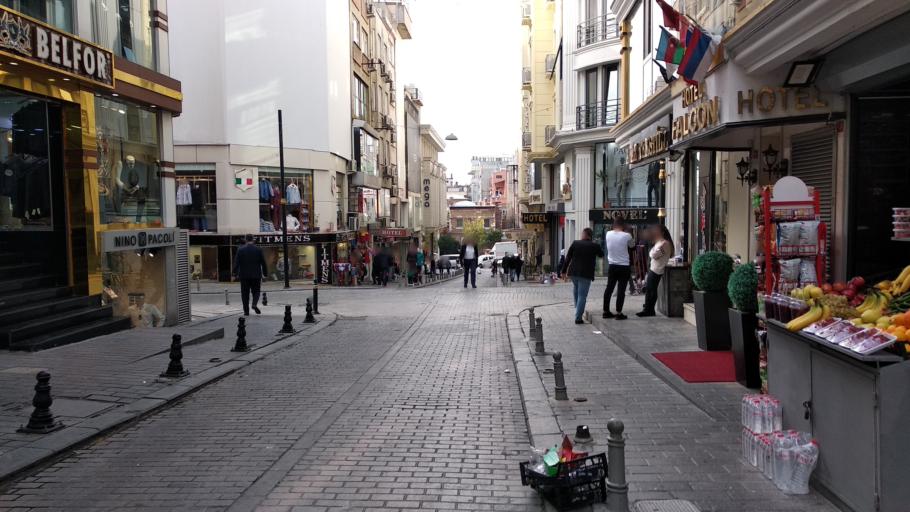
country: TR
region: Istanbul
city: Istanbul
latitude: 41.0110
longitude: 28.9586
